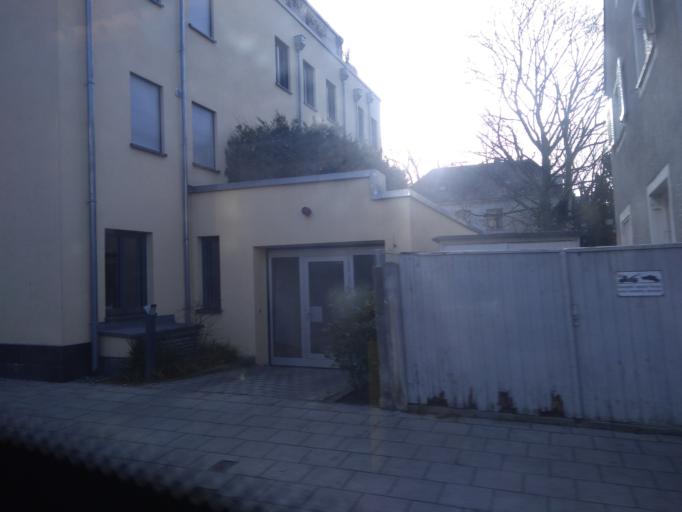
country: DE
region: Bavaria
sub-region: Upper Bavaria
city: Bogenhausen
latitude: 48.1656
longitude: 11.5921
